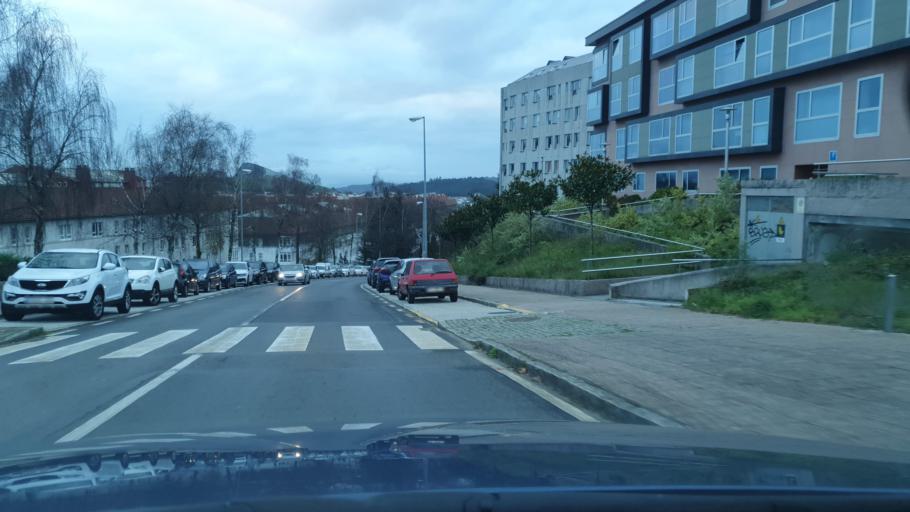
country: ES
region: Galicia
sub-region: Provincia da Coruna
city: Santiago de Compostela
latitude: 42.8859
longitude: -8.5277
